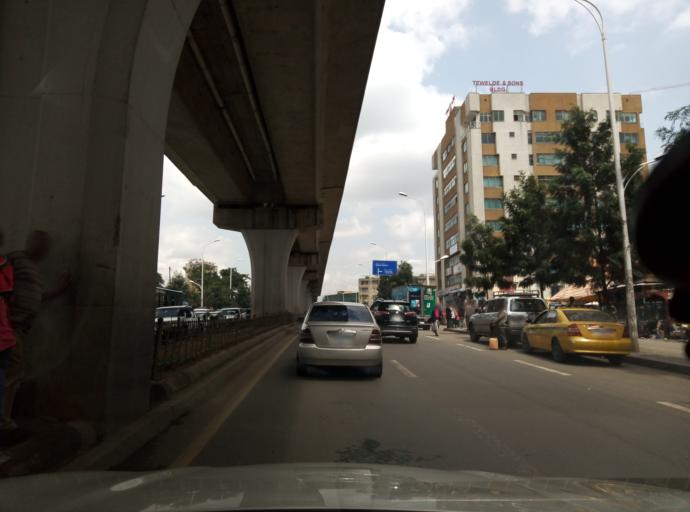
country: ET
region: Adis Abeba
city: Addis Ababa
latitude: 9.0116
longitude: 38.7516
